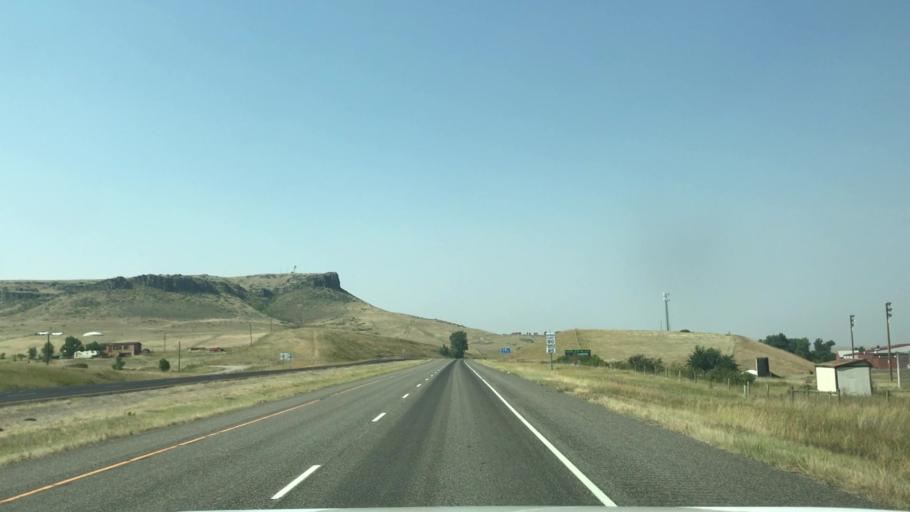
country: US
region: Montana
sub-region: Cascade County
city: Sun Prairie
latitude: 47.2687
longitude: -111.7079
